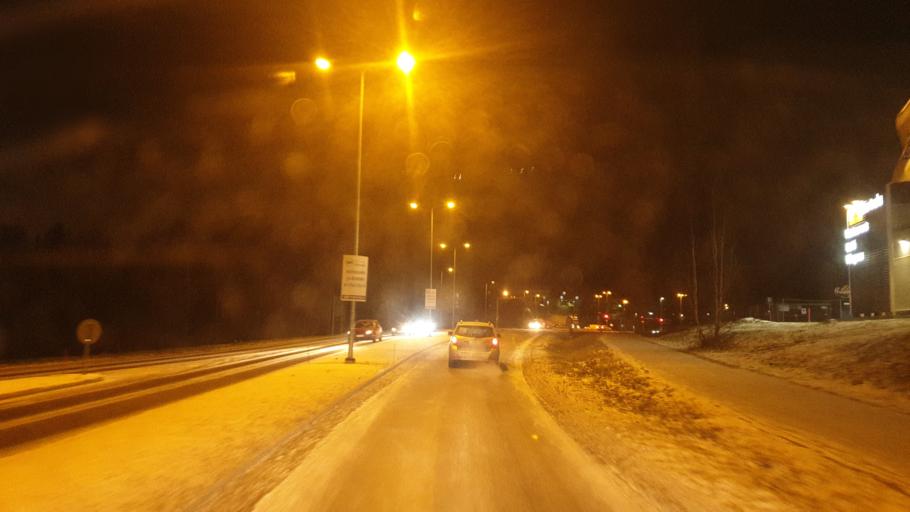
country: FI
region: Southern Savonia
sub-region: Savonlinna
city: Savonlinna
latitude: 61.8657
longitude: 28.9413
